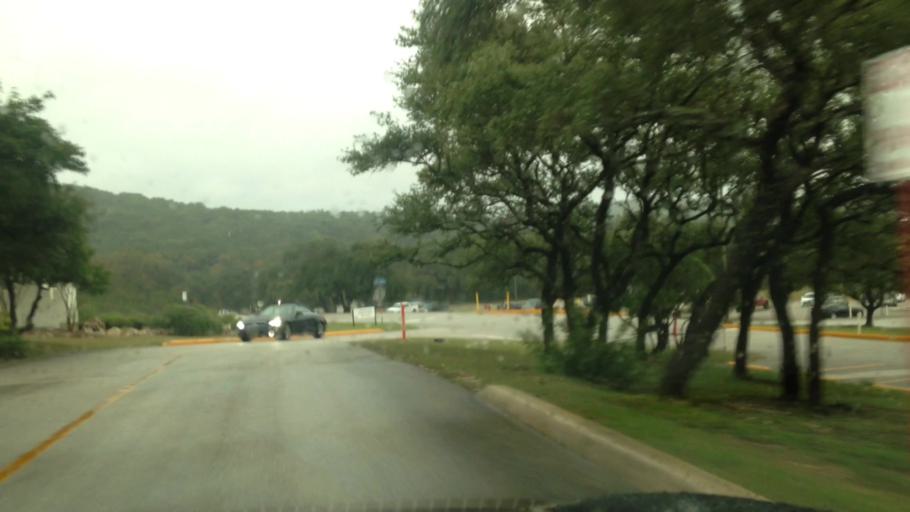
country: US
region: Texas
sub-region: Bexar County
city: Cross Mountain
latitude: 29.6379
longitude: -98.6028
